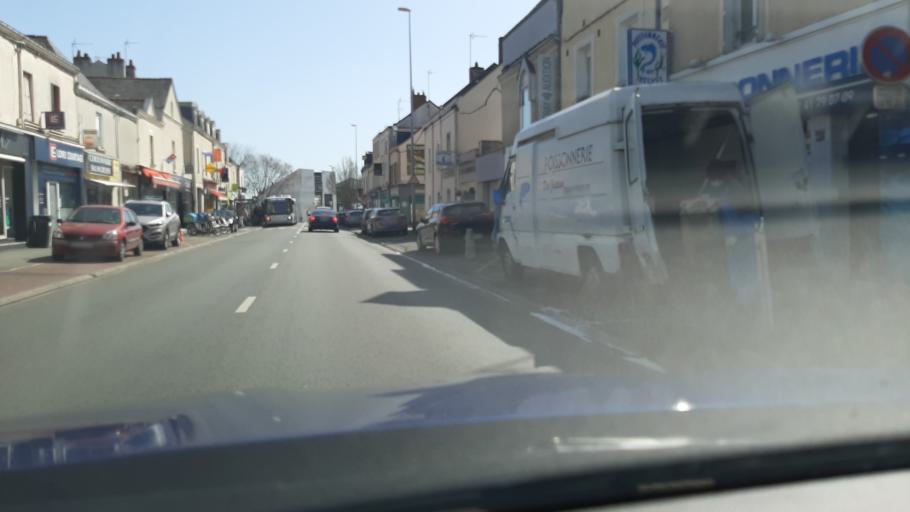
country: FR
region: Pays de la Loire
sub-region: Departement de Maine-et-Loire
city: Angers
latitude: 47.4540
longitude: -0.5273
